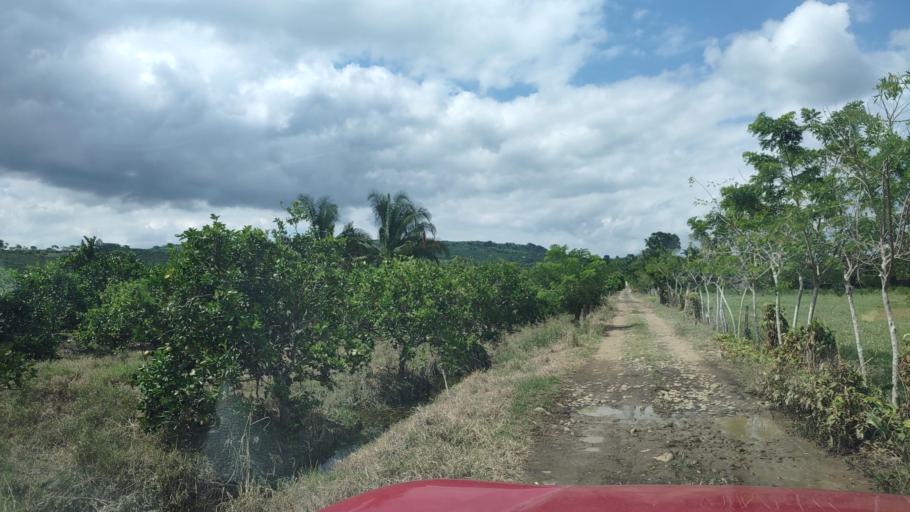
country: MX
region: Puebla
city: San Jose Acateno
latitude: 20.2208
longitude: -97.1456
